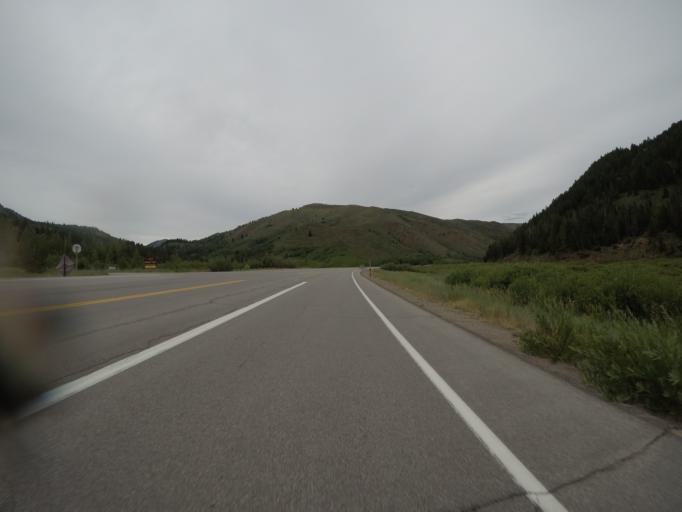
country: US
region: Wyoming
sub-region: Lincoln County
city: Afton
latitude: 42.4848
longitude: -110.9615
